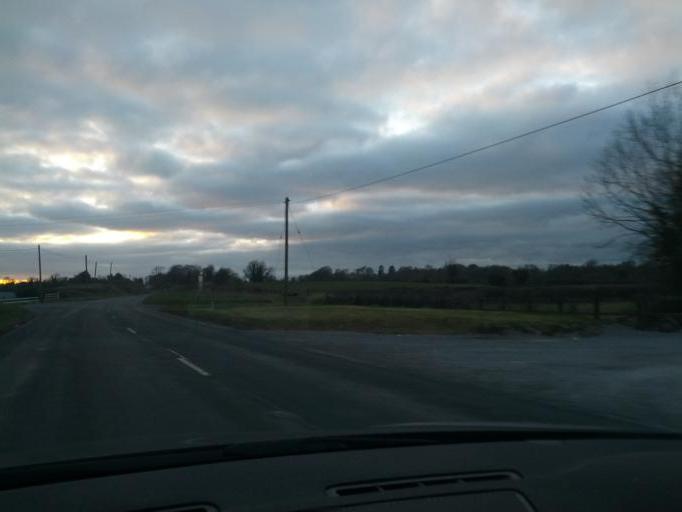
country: IE
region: Leinster
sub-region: Uibh Fhaili
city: Birr
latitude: 53.1000
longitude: -7.9824
